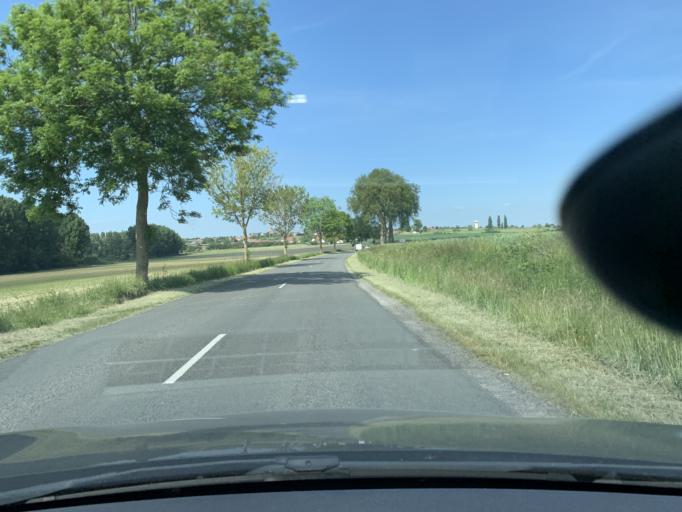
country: FR
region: Nord-Pas-de-Calais
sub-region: Departement du Pas-de-Calais
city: Oisy-le-Verger
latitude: 50.2382
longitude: 3.1102
